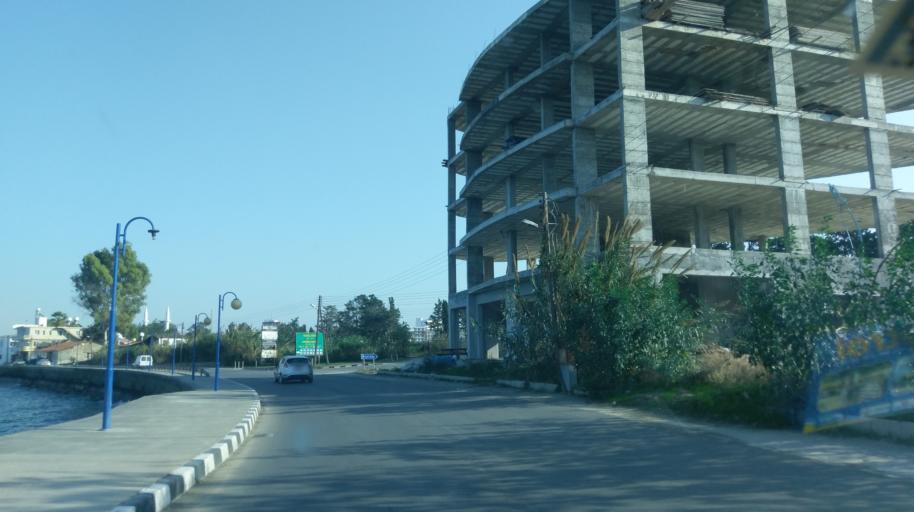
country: CY
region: Lefkosia
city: Lefka
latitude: 35.1411
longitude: 32.8240
